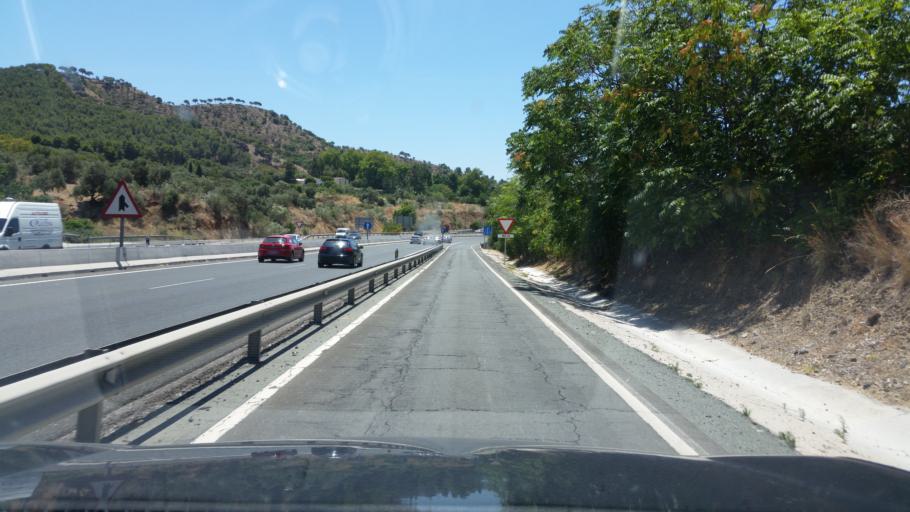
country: ES
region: Andalusia
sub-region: Provincia de Malaga
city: Malaga
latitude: 36.7685
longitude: -4.4249
